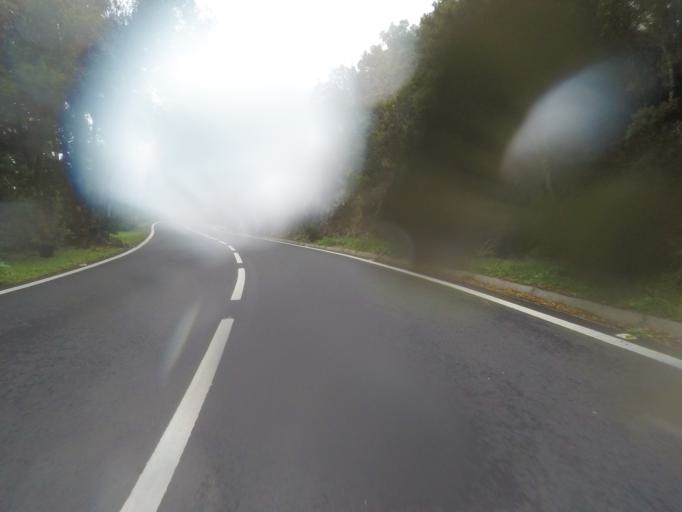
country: ES
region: Canary Islands
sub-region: Provincia de Santa Cruz de Tenerife
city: Vallehermosa
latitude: 28.1288
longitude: -17.2688
